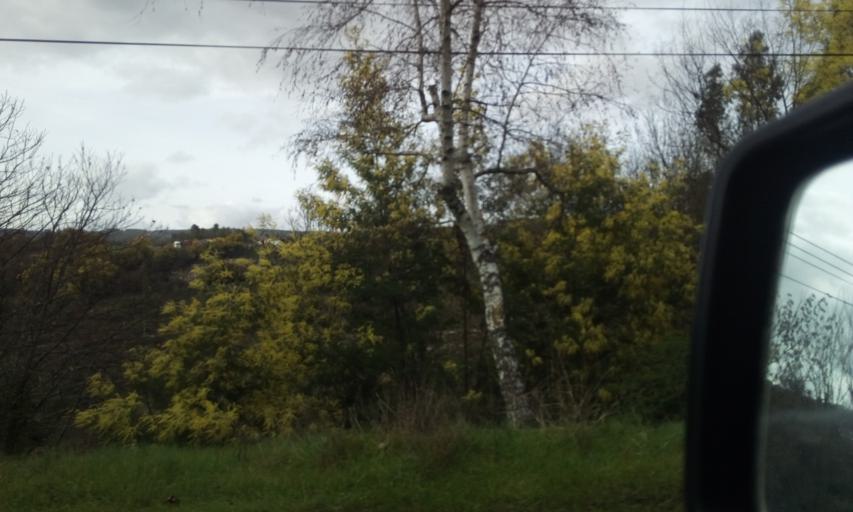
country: PT
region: Guarda
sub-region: Fornos de Algodres
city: Fornos de Algodres
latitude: 40.6143
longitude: -7.5105
